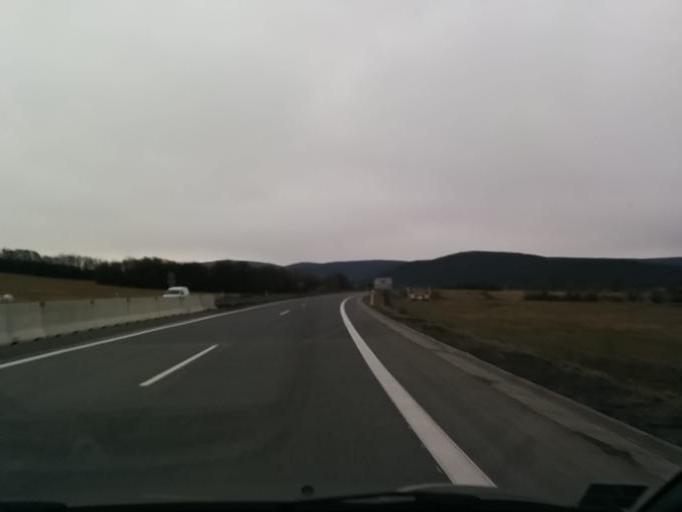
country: SK
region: Nitriansky
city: Tlmace
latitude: 48.3710
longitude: 18.5365
